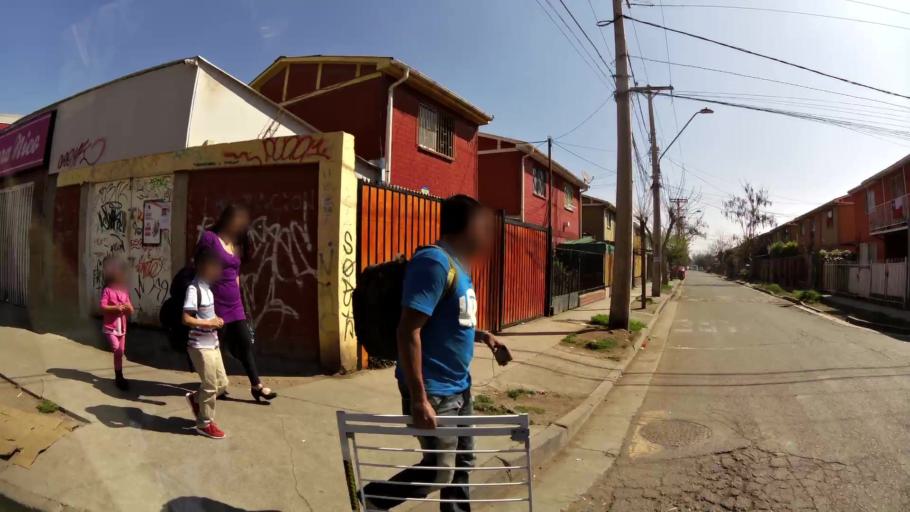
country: CL
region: Santiago Metropolitan
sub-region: Provincia de Santiago
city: Lo Prado
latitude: -33.3533
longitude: -70.7468
